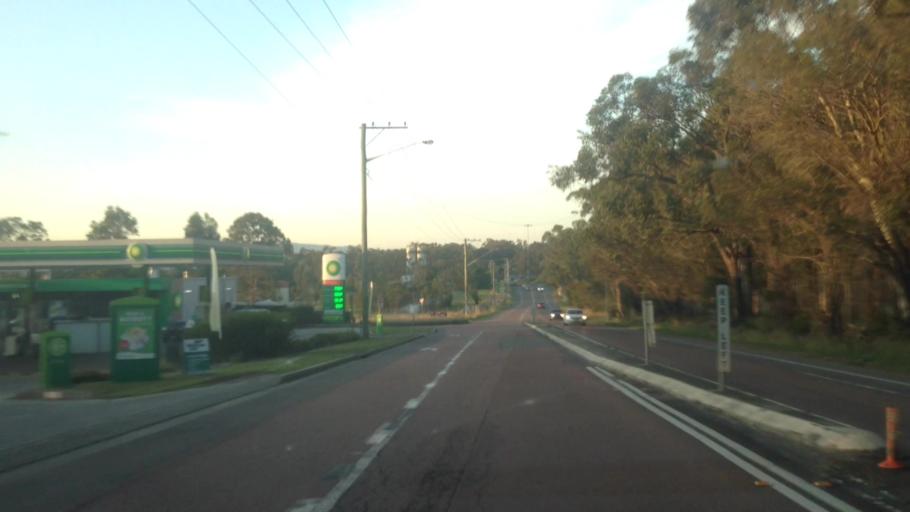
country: AU
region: New South Wales
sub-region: Lake Macquarie Shire
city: Dora Creek
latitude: -33.1168
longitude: 151.4782
